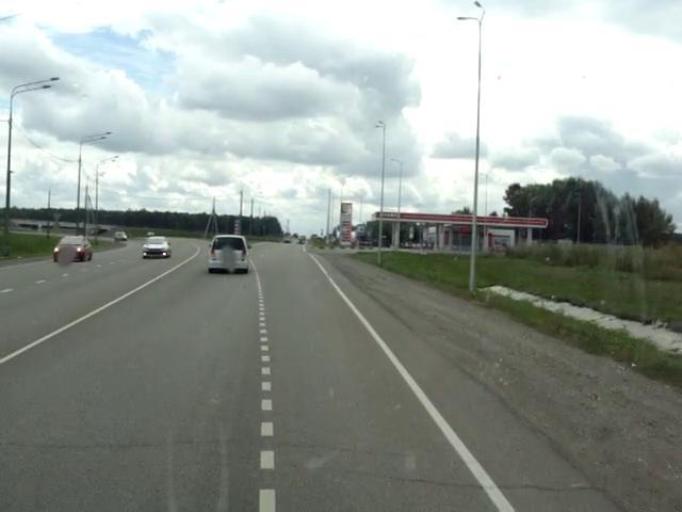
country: RU
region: Altai Krai
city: Zarya
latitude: 52.5807
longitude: 85.1756
